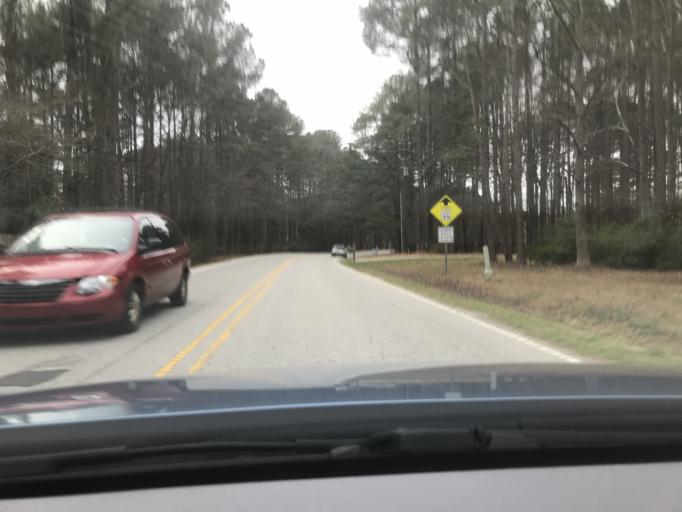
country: US
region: North Carolina
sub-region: Wake County
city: Apex
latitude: 35.7162
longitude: -78.7915
